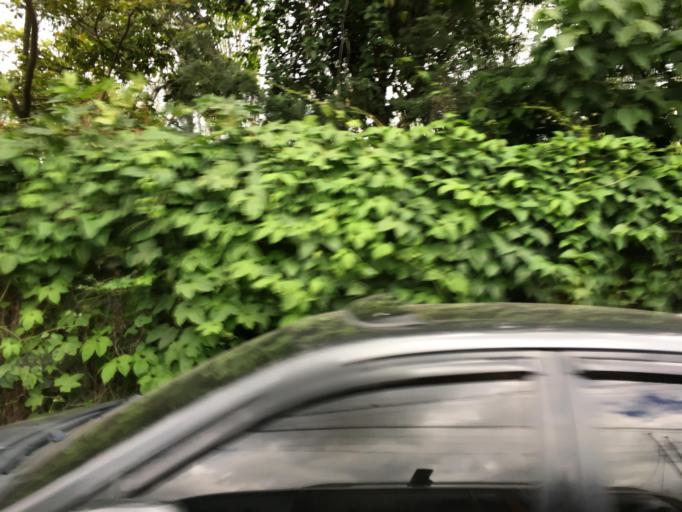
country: GT
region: Sacatepequez
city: Antigua Guatemala
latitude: 14.5683
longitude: -90.7419
